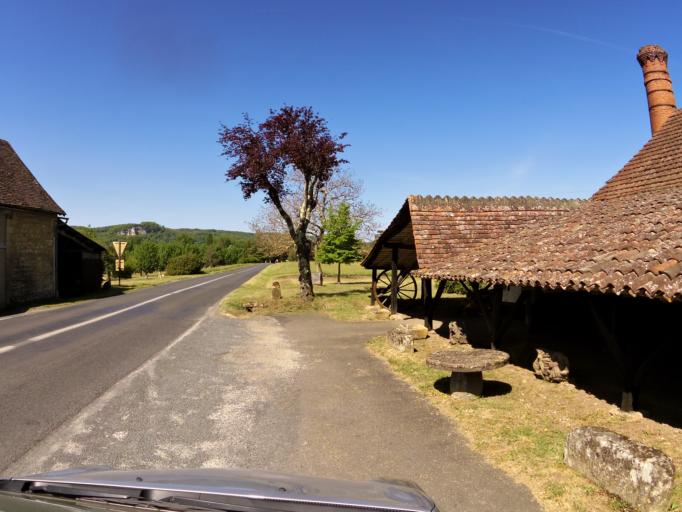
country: FR
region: Aquitaine
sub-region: Departement de la Dordogne
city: Cenac-et-Saint-Julien
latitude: 44.8087
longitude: 1.2031
